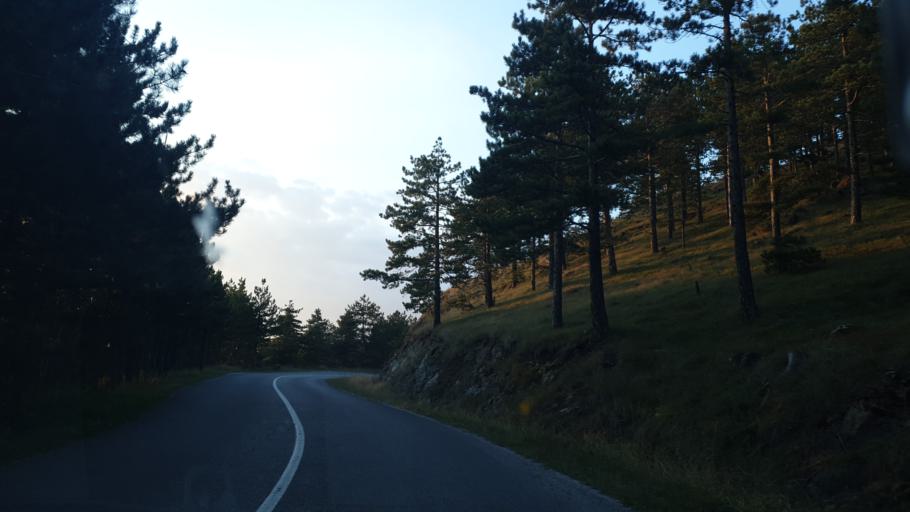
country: RS
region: Central Serbia
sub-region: Zlatiborski Okrug
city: Kosjeric
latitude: 44.0880
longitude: 19.9941
